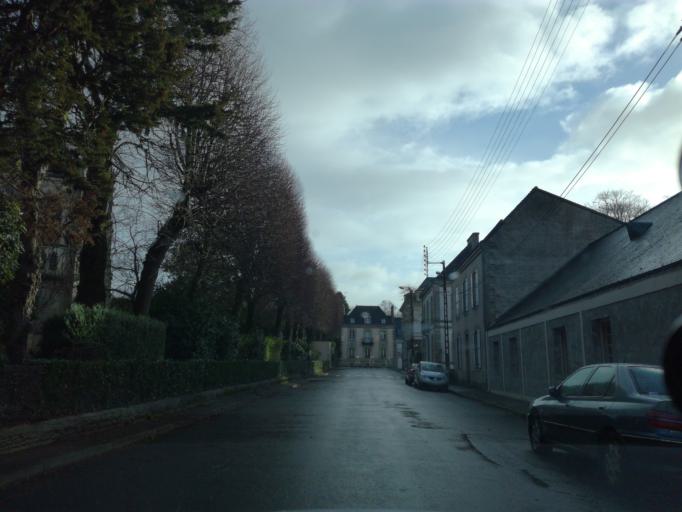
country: FR
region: Brittany
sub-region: Departement du Morbihan
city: Pontivy
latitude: 48.0627
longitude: -2.9684
